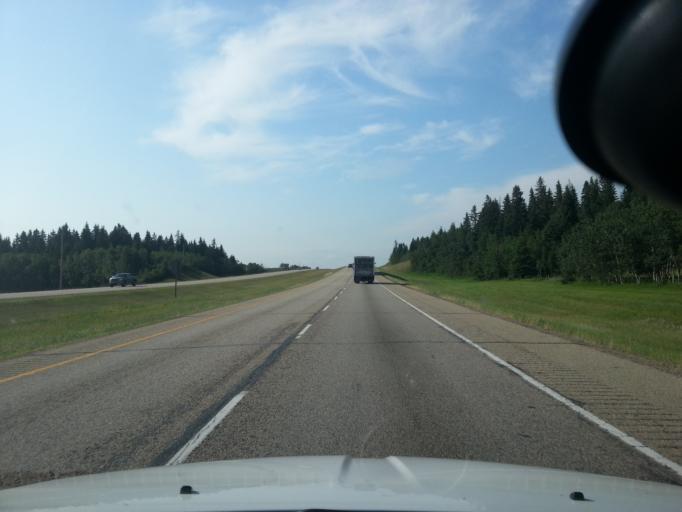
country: CA
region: Alberta
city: Ponoka
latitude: 52.5961
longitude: -113.6634
